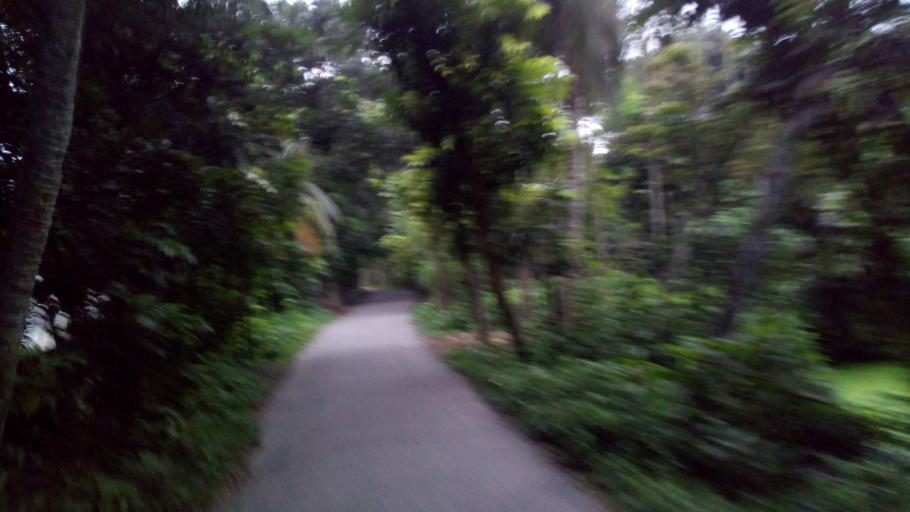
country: BD
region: Khulna
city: Phultala
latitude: 22.7564
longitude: 89.4082
